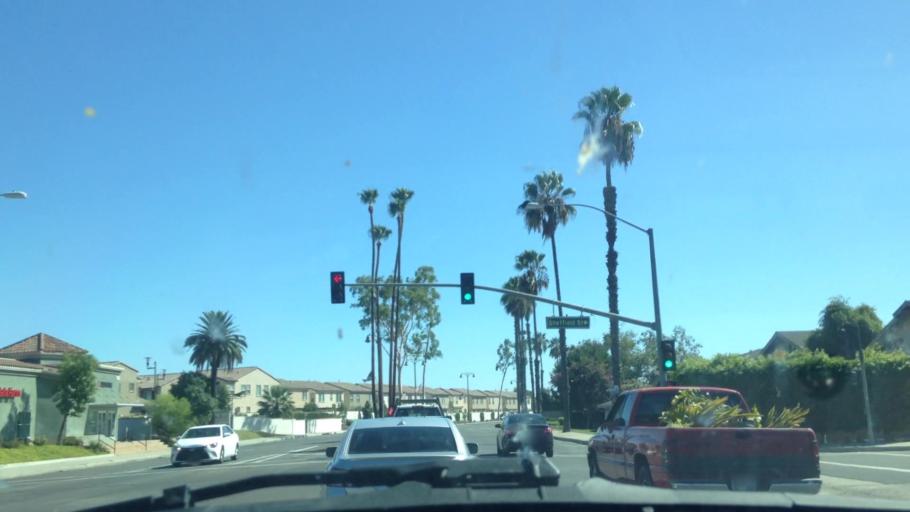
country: US
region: California
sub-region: Orange County
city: Placentia
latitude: 33.8853
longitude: -117.8629
